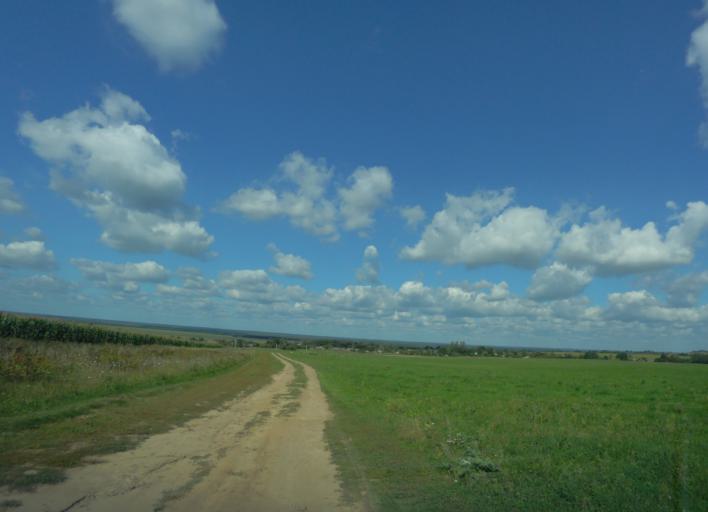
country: BY
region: Minsk
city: Zyembin
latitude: 54.3851
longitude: 28.3876
